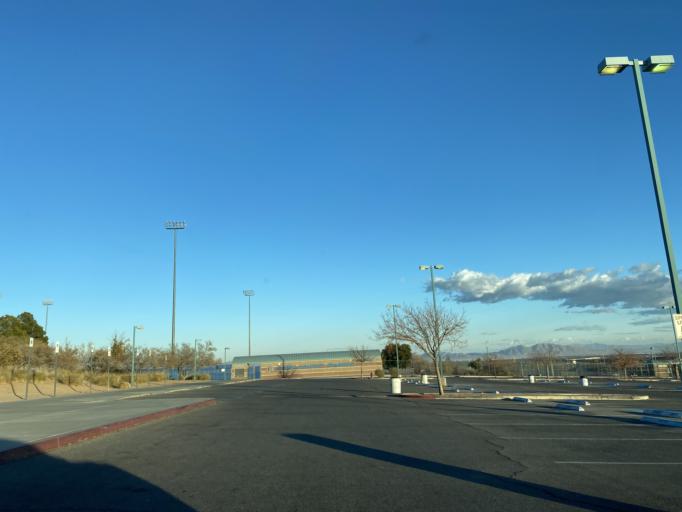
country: US
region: Nevada
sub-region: Clark County
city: Summerlin South
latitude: 36.2783
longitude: -115.3189
